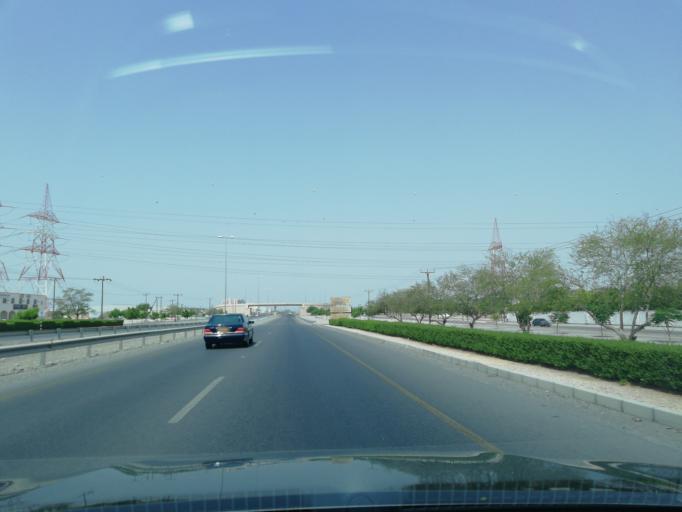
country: OM
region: Al Batinah
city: Barka'
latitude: 23.6799
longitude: 58.0066
